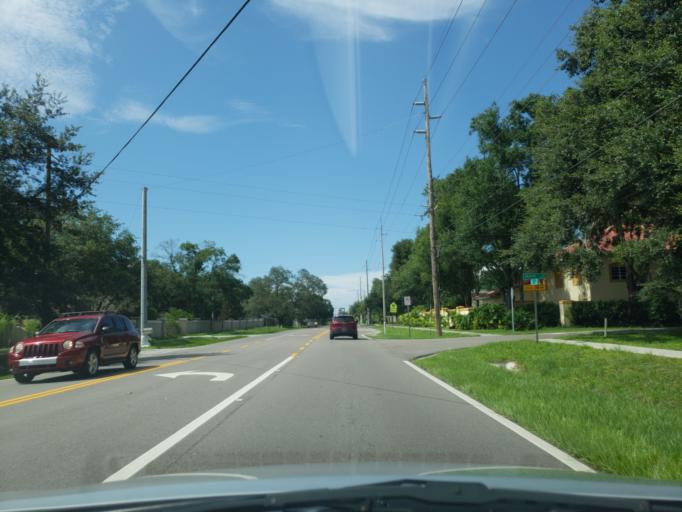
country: US
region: Florida
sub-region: Hillsborough County
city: Carrollwood Village
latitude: 28.0657
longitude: -82.5416
